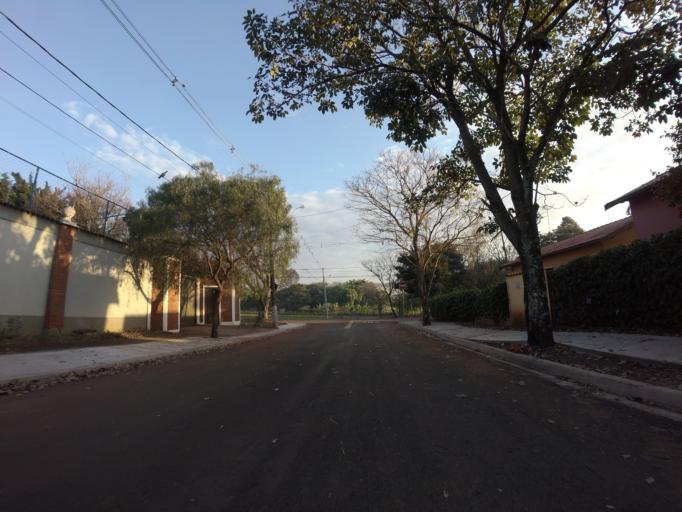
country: BR
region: Sao Paulo
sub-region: Piracicaba
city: Piracicaba
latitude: -22.7593
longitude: -47.5885
